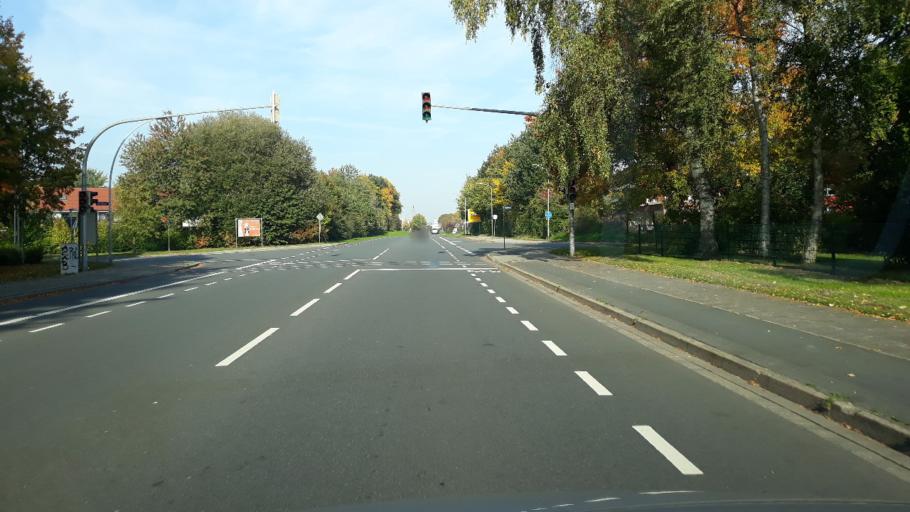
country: DE
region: Schleswig-Holstein
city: Schleswig
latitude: 54.5282
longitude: 9.5716
